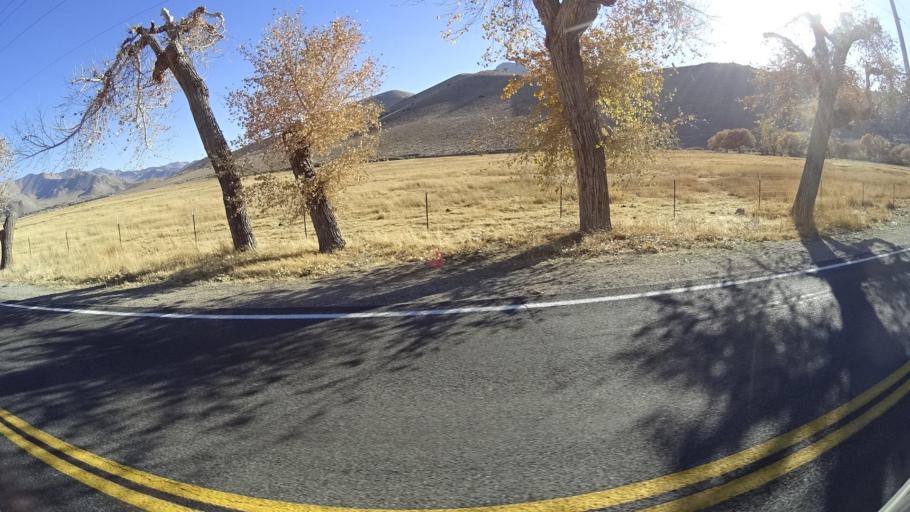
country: US
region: California
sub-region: Kern County
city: Weldon
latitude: 35.6653
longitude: -118.2995
